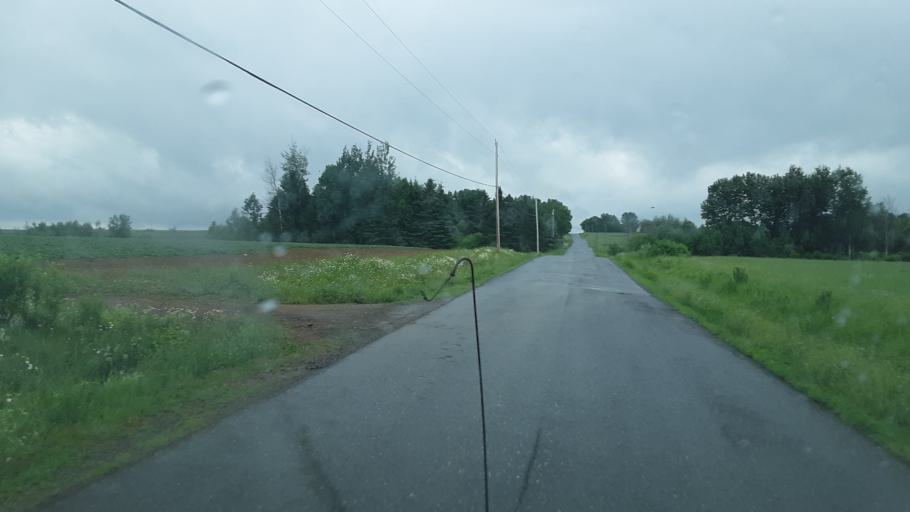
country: US
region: Maine
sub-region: Aroostook County
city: Presque Isle
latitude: 46.6816
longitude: -68.1968
